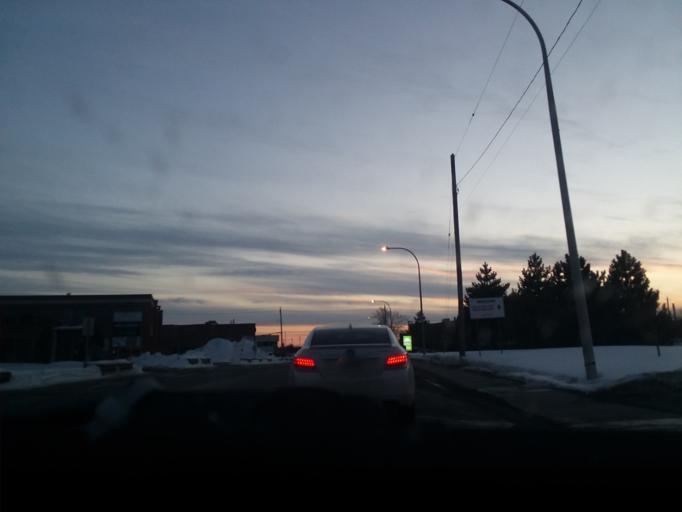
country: CA
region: Quebec
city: Saint-Raymond
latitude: 45.4455
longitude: -73.6240
